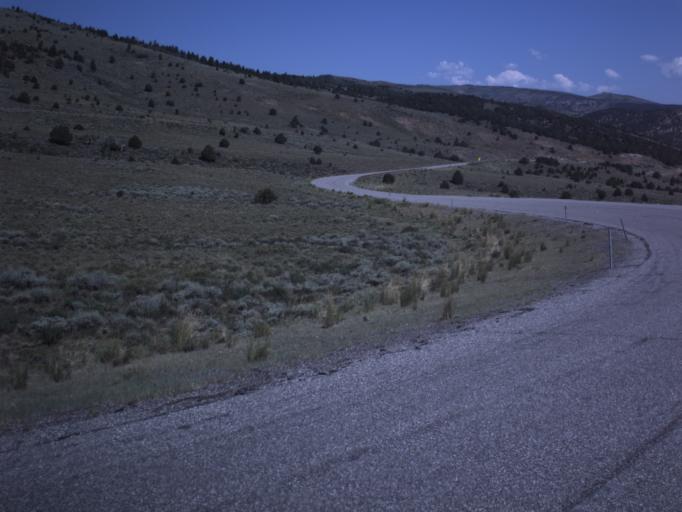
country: US
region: Utah
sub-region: Wayne County
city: Loa
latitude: 38.6007
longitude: -111.4606
